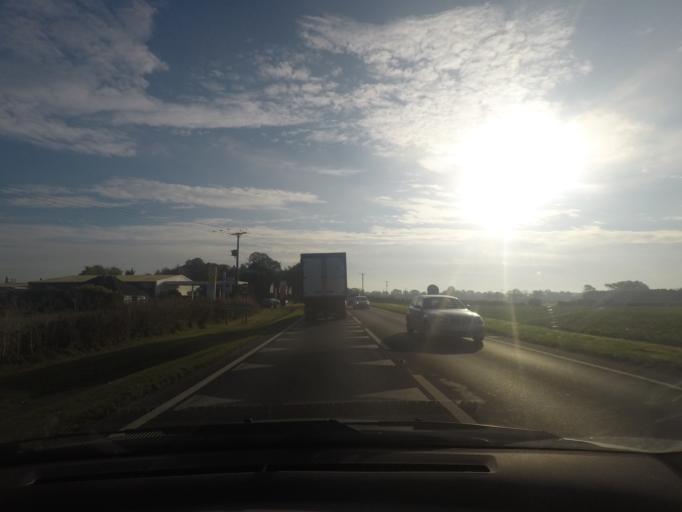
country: GB
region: England
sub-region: East Riding of Yorkshire
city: Londesborough
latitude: 53.8806
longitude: -0.7150
